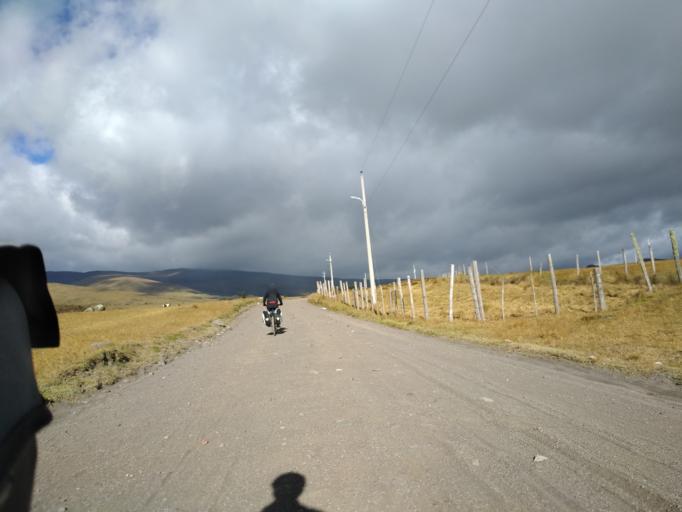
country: EC
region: Pichincha
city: Machachi
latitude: -0.5601
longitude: -78.4500
